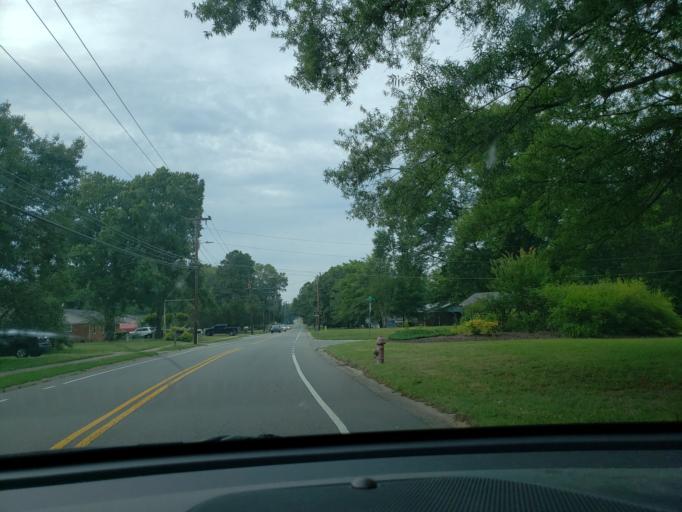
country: US
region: North Carolina
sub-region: Durham County
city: Durham
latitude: 35.9004
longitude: -78.9113
